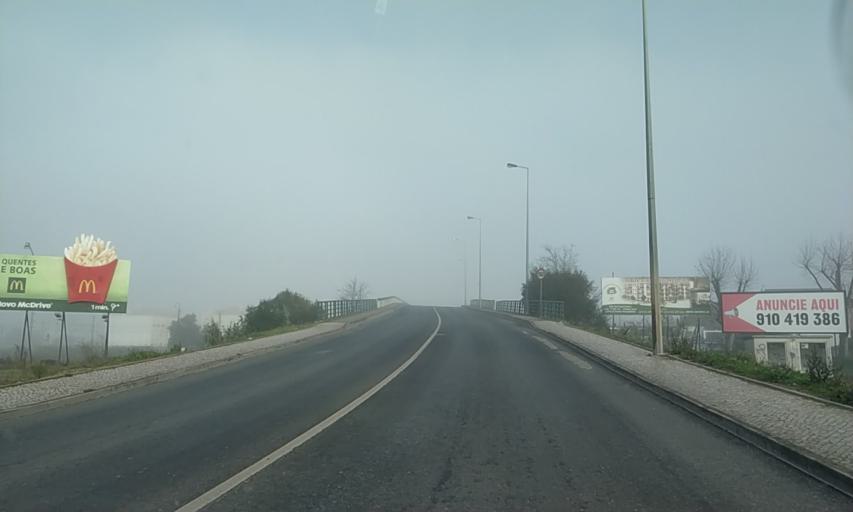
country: PT
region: Setubal
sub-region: Palmela
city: Pinhal Novo
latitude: 38.6288
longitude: -8.9177
